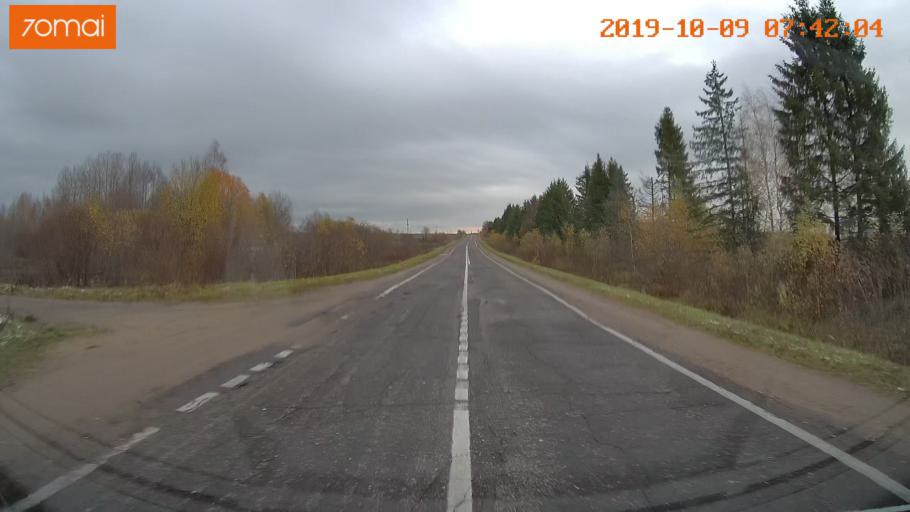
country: RU
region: Jaroslavl
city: Kukoboy
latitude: 58.6414
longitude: 39.7164
